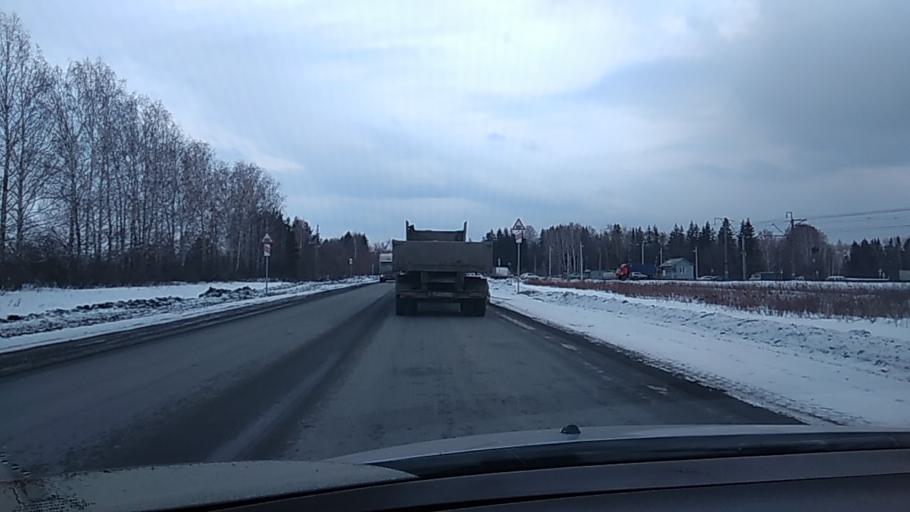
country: RU
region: Sverdlovsk
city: Sovkhoznyy
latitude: 56.6040
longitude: 61.3021
